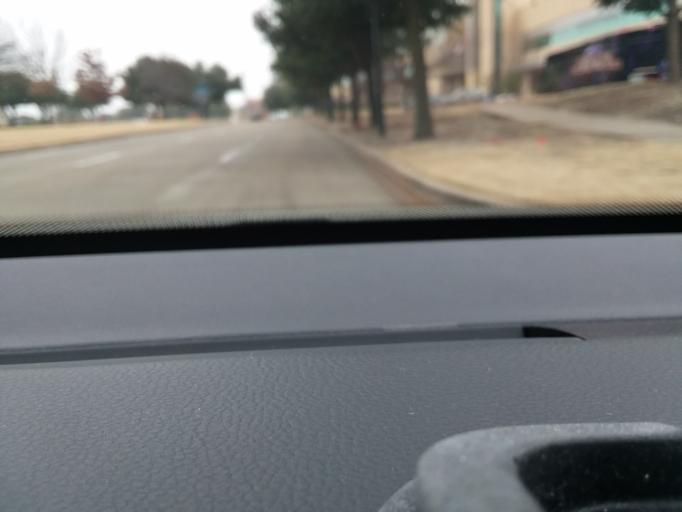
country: US
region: Texas
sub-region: Collin County
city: Frisco
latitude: 33.1016
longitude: -96.8204
